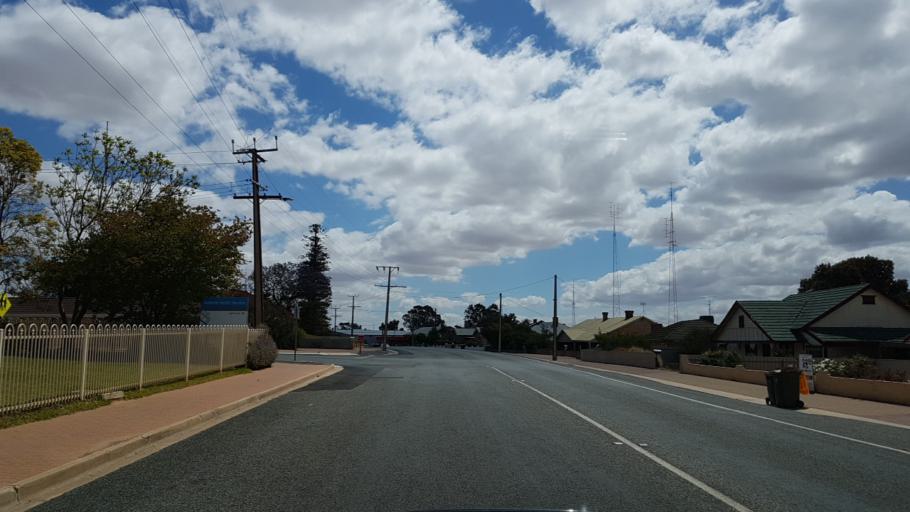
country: AU
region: South Australia
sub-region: Loxton Waikerie
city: Waikerie
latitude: -34.1818
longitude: 139.9847
